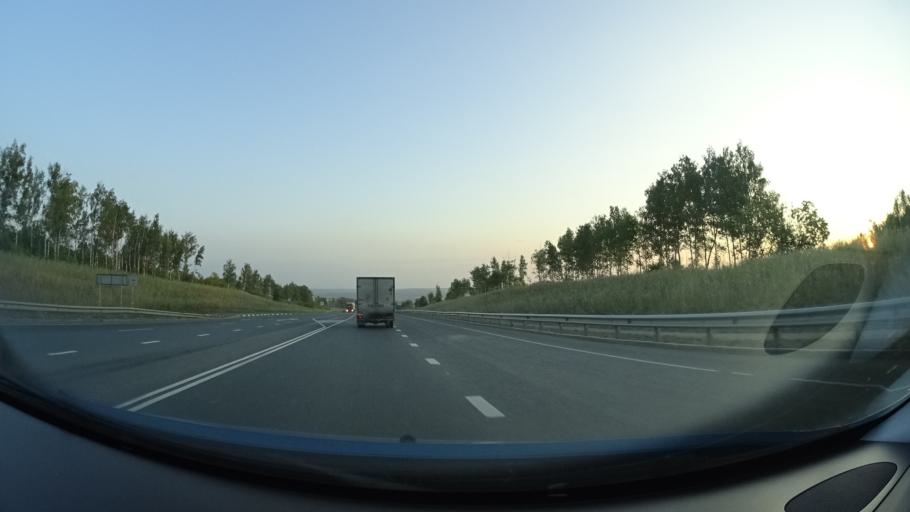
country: RU
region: Samara
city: Sernovodsk
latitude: 53.9113
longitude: 51.2967
